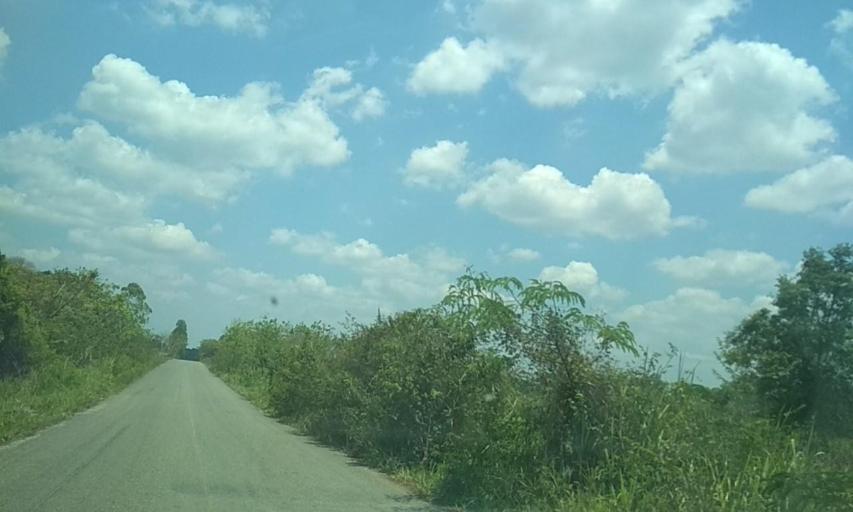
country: MX
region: Tabasco
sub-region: Huimanguillo
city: Francisco Rueda
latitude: 17.7785
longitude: -93.8263
